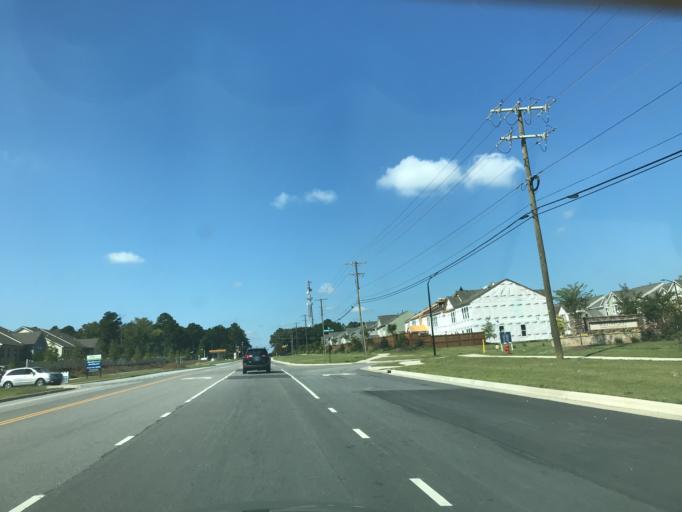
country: US
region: North Carolina
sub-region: Durham County
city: Durham
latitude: 35.9045
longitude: -78.9138
